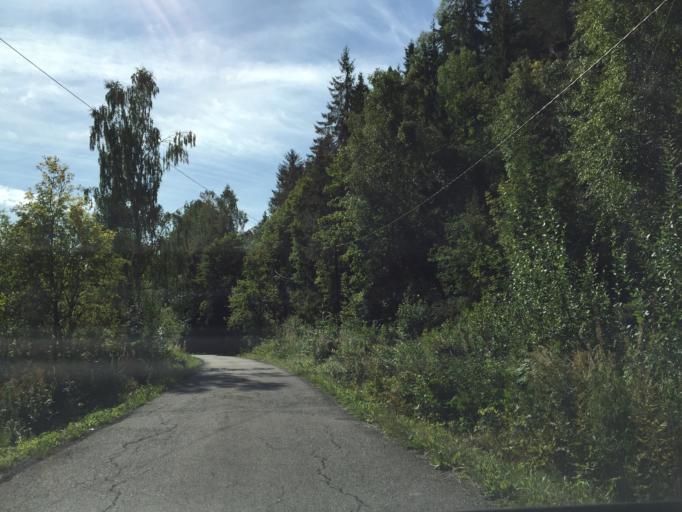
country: NO
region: Vestfold
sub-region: Hof
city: Hof
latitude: 59.4689
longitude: 10.1445
